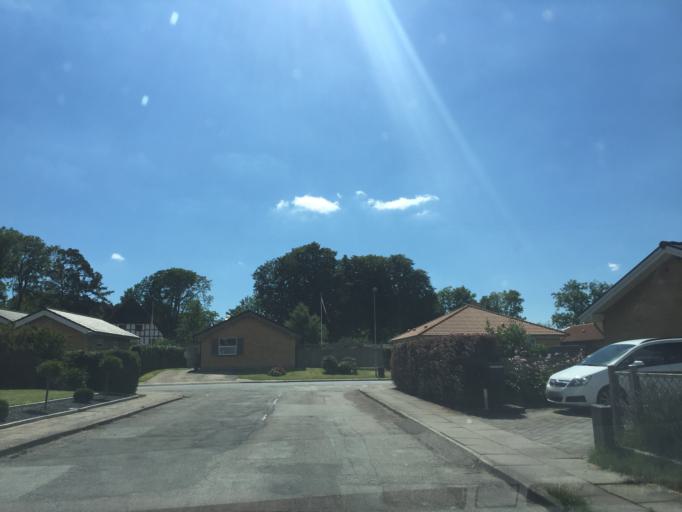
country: DK
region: South Denmark
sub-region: Odense Kommune
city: Hojby
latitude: 55.3438
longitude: 10.4247
